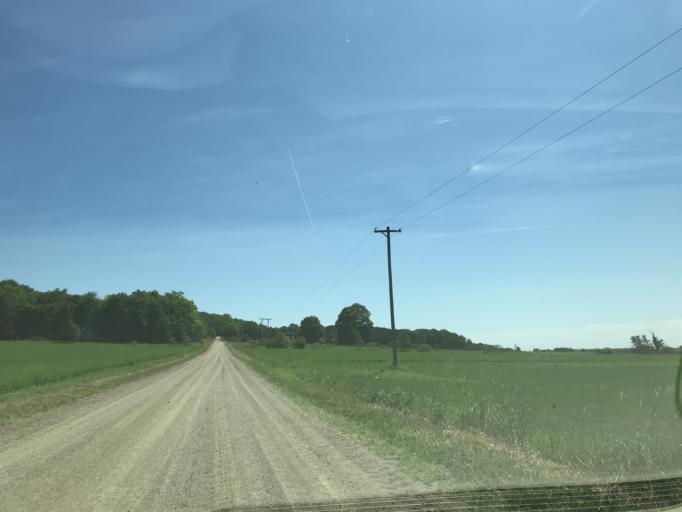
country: US
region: Michigan
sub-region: Missaukee County
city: Lake City
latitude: 44.2791
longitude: -85.0465
